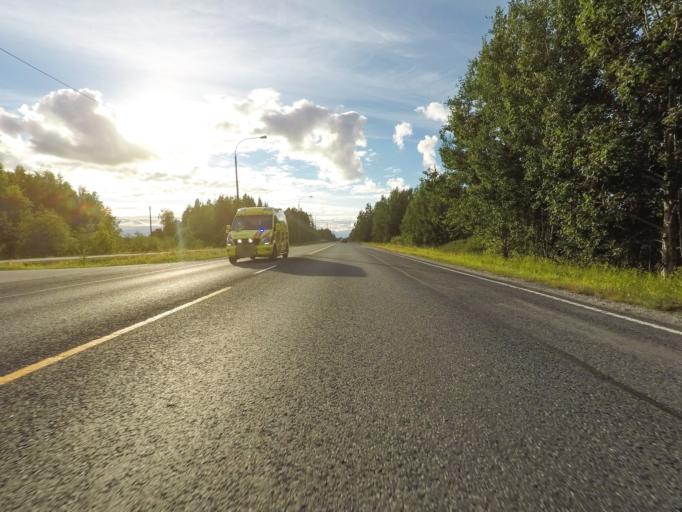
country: FI
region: Northern Savo
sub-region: Kuopio
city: Kuopio
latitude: 62.9514
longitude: 27.8785
